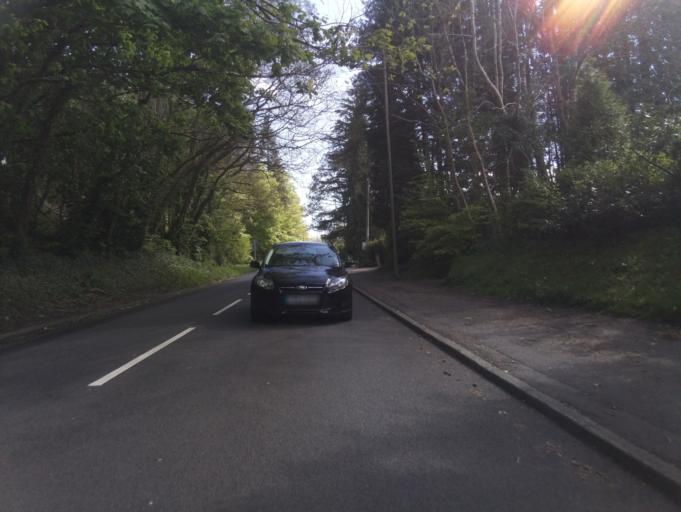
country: GB
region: Wales
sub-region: Caerphilly County Borough
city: Caerphilly
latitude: 51.5667
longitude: -3.2166
